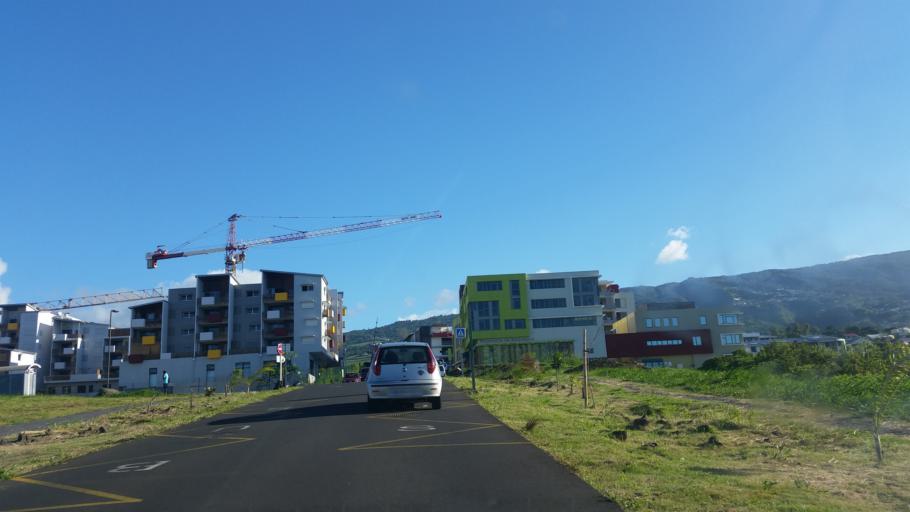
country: RE
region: Reunion
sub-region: Reunion
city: Sainte-Marie
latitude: -20.9190
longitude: 55.5282
